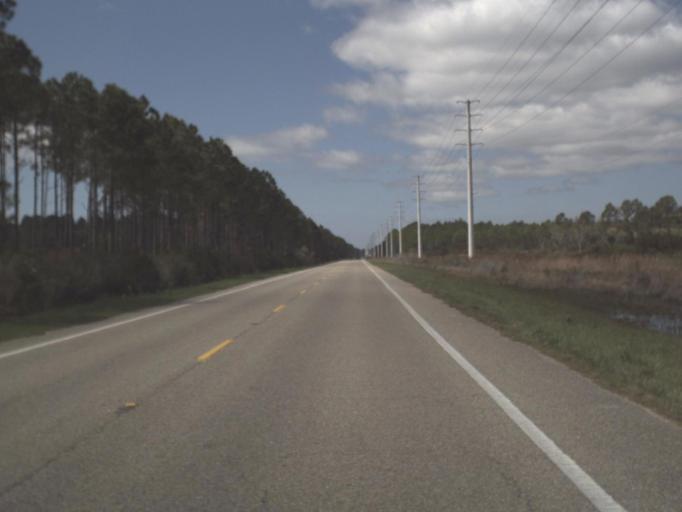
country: US
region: Florida
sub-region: Franklin County
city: Apalachicola
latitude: 29.7242
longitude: -85.0932
